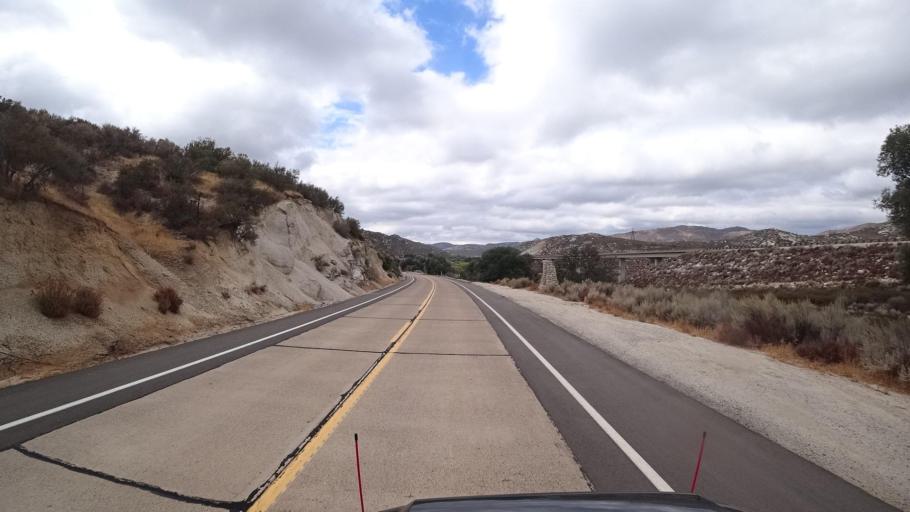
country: US
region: California
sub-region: San Diego County
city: Campo
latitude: 32.7255
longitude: -116.4240
